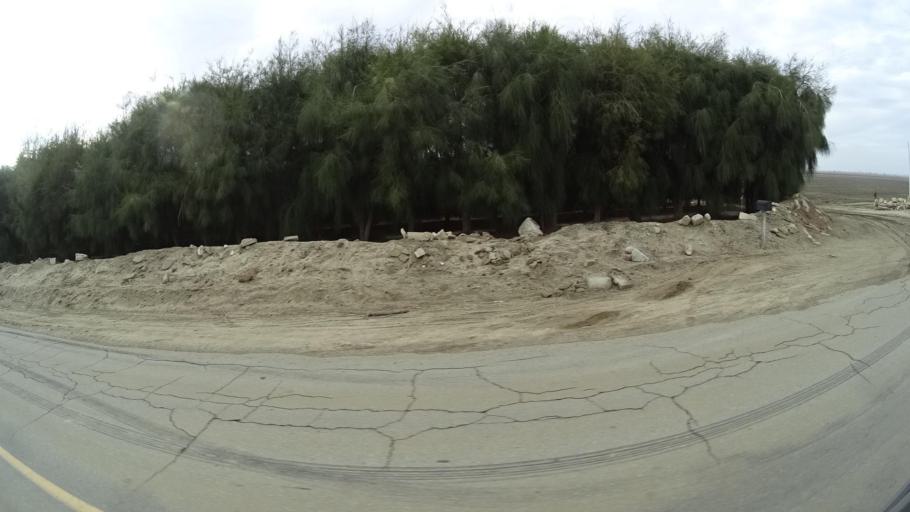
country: US
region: California
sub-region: Kern County
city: Arvin
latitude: 35.1581
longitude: -118.8236
